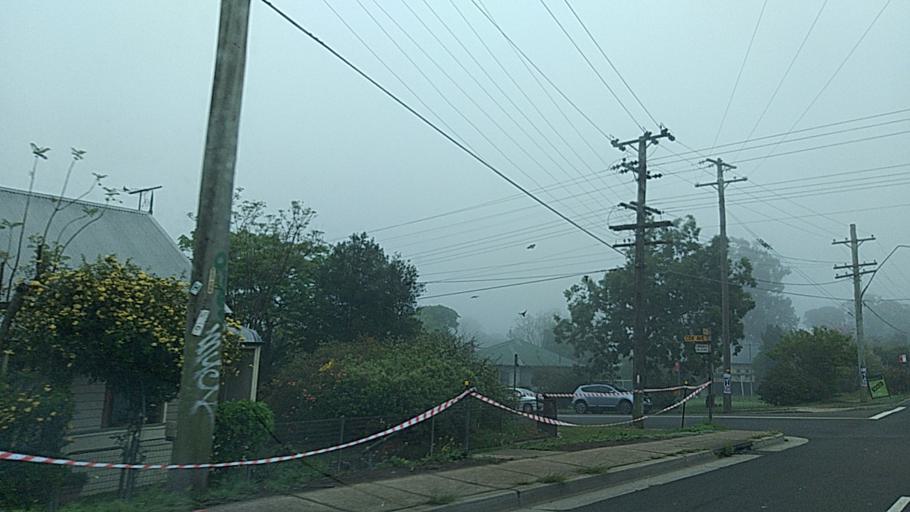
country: AU
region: New South Wales
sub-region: Penrith Municipality
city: Kingswood Park
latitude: -33.7559
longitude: 150.7123
